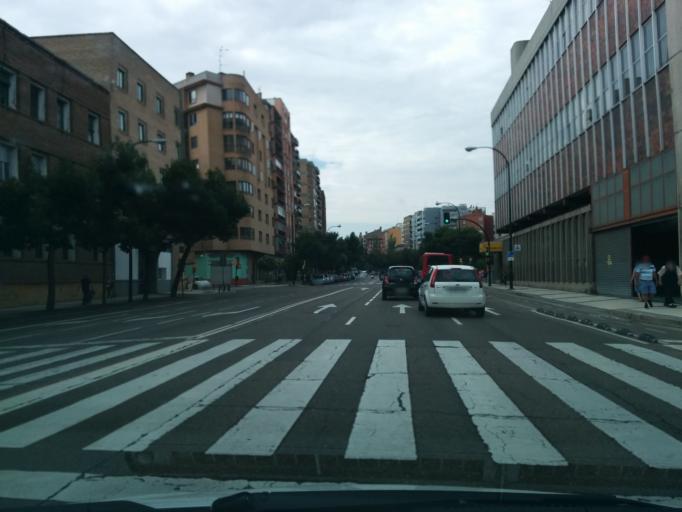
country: ES
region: Aragon
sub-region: Provincia de Zaragoza
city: Almozara
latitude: 41.6515
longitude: -0.8937
